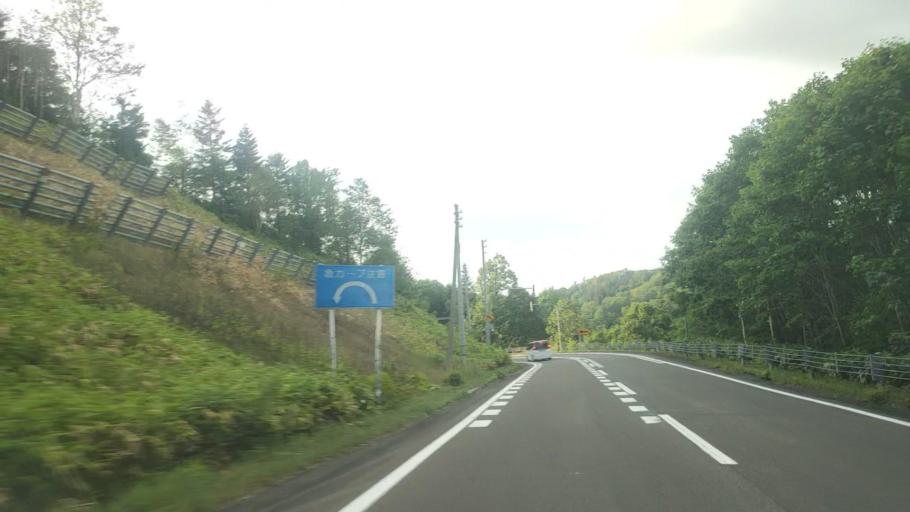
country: JP
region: Hokkaido
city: Bibai
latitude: 43.1686
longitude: 142.0785
